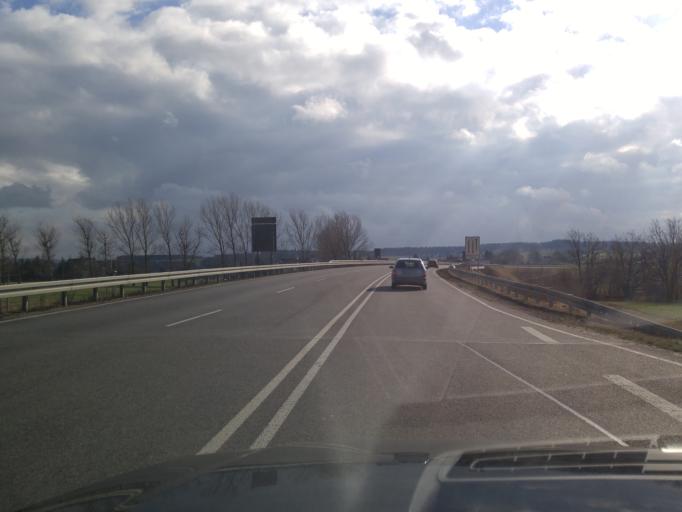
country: DE
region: Saxony
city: Lichtentanne
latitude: 50.6670
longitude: 12.4440
